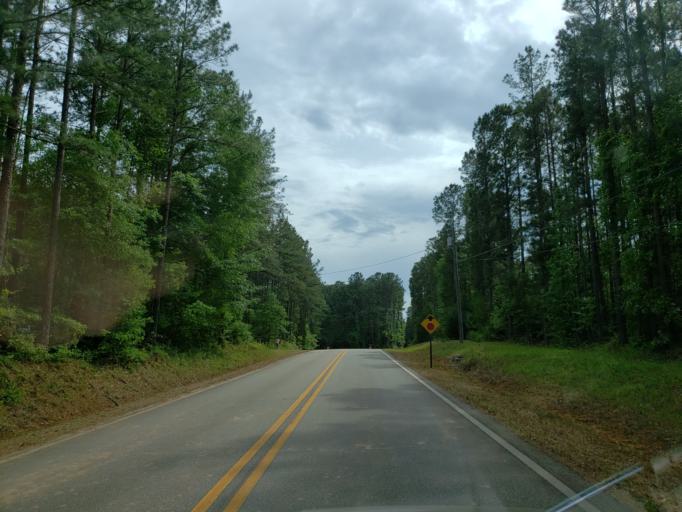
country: US
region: Georgia
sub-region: Monroe County
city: Forsyth
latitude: 32.9420
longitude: -83.9375
